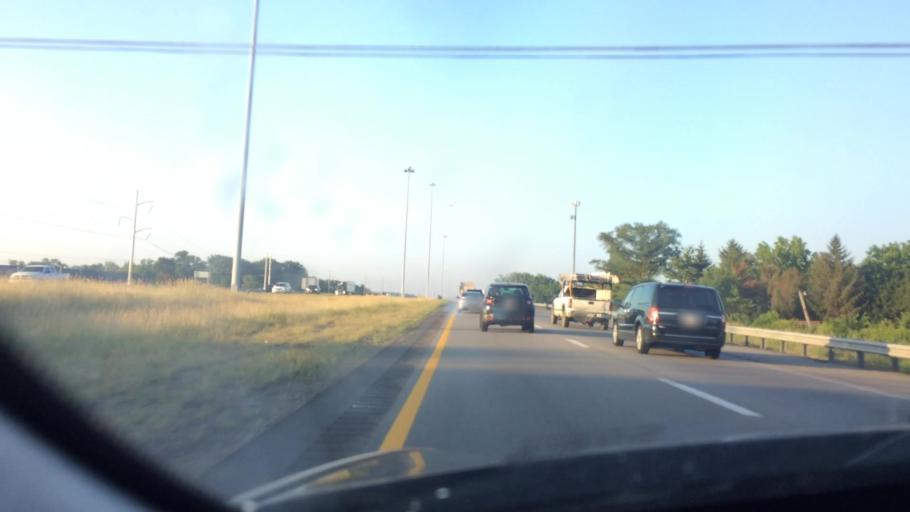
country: US
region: Ohio
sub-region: Lucas County
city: Holland
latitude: 41.5953
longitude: -83.6924
